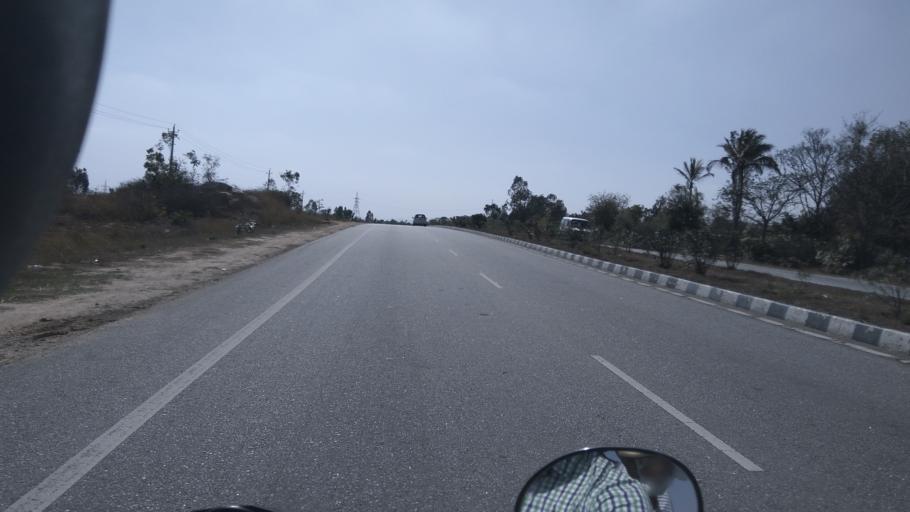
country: IN
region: Karnataka
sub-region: Kolar
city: Mulbagal
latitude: 13.1526
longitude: 78.3190
